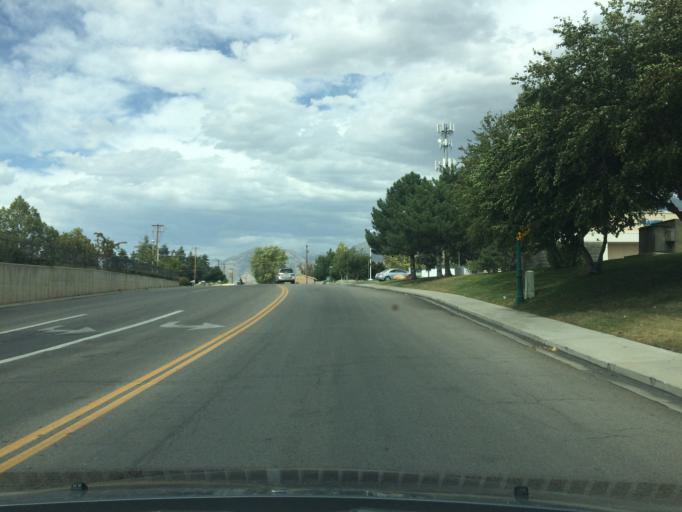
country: US
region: Utah
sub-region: Utah County
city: Orem
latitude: 40.2738
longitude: -111.7045
